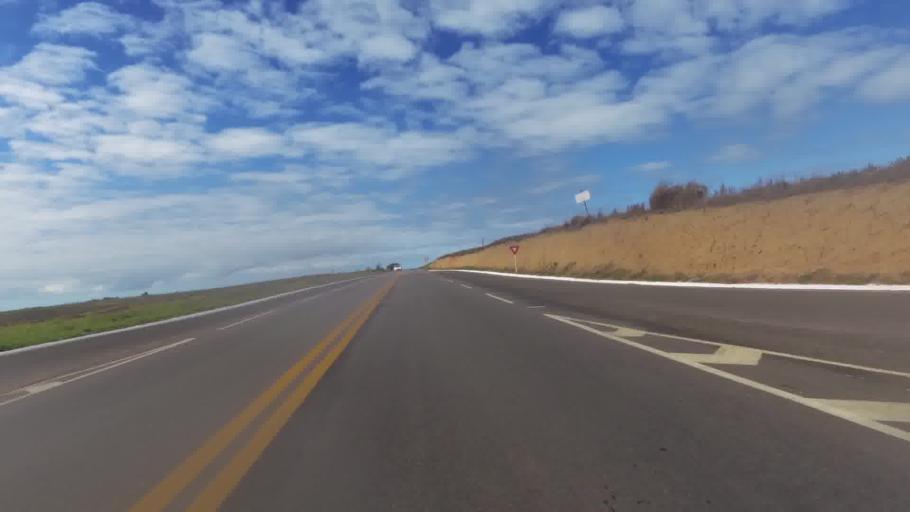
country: BR
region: Espirito Santo
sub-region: Marataizes
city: Marataizes
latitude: -21.0891
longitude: -40.8492
